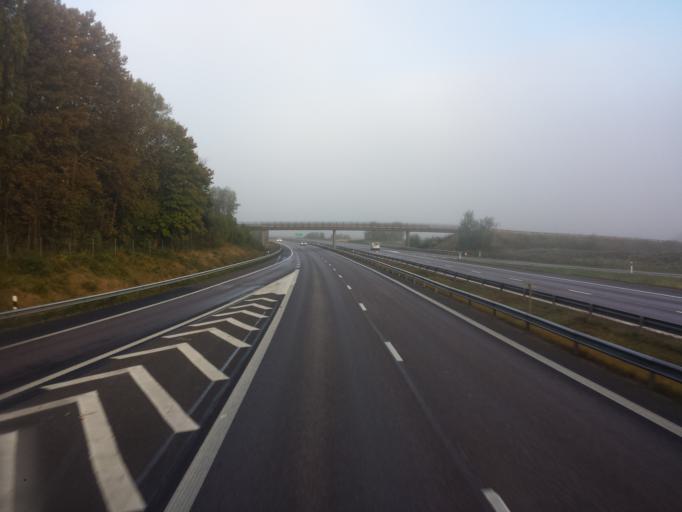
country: SE
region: Halland
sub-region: Kungsbacka Kommun
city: Fjaeras kyrkby
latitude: 57.4320
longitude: 12.1538
